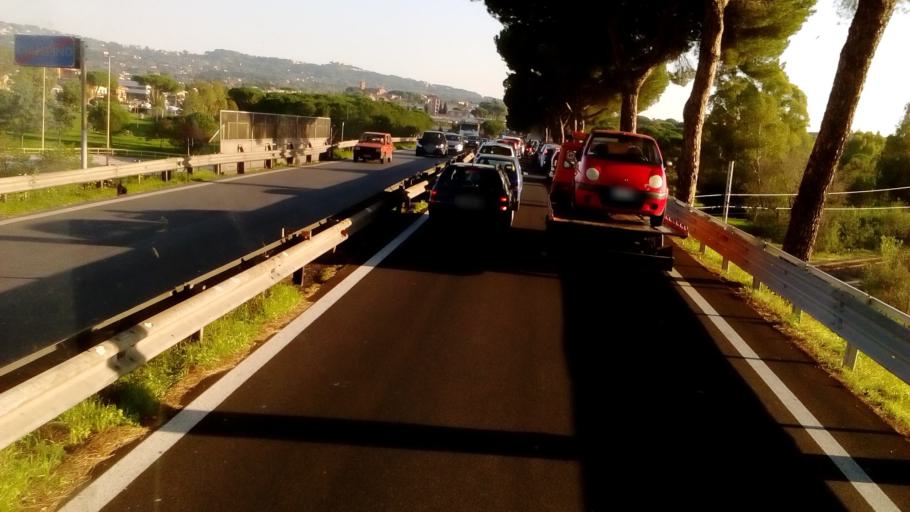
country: IT
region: Latium
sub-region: Citta metropolitana di Roma Capitale
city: Ciampino
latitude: 41.7774
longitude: 12.6063
